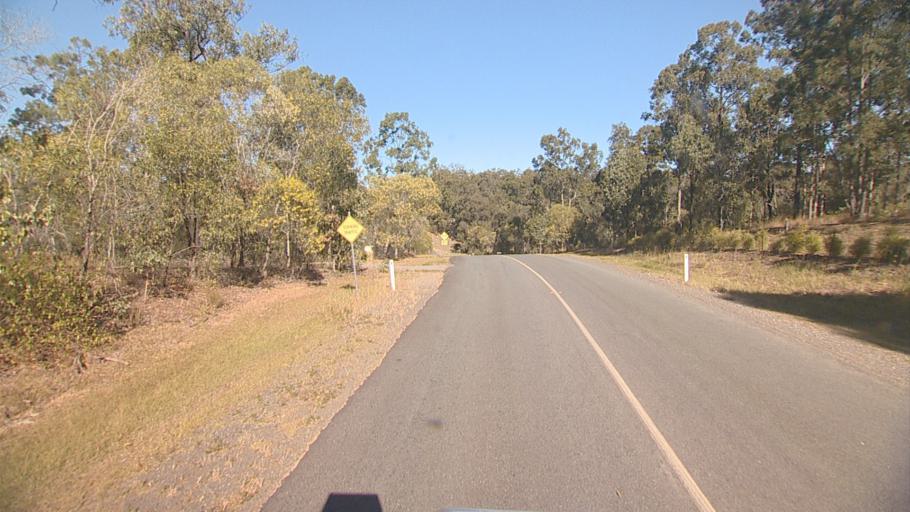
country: AU
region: Queensland
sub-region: Ipswich
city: Springfield Lakes
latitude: -27.7134
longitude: 152.9176
